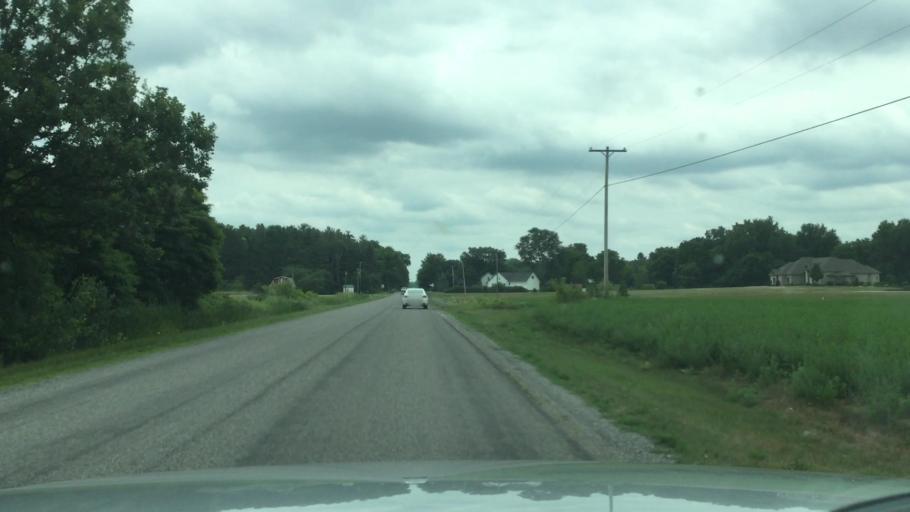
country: US
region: Michigan
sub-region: Saginaw County
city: Frankenmuth
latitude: 43.3217
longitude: -83.7907
